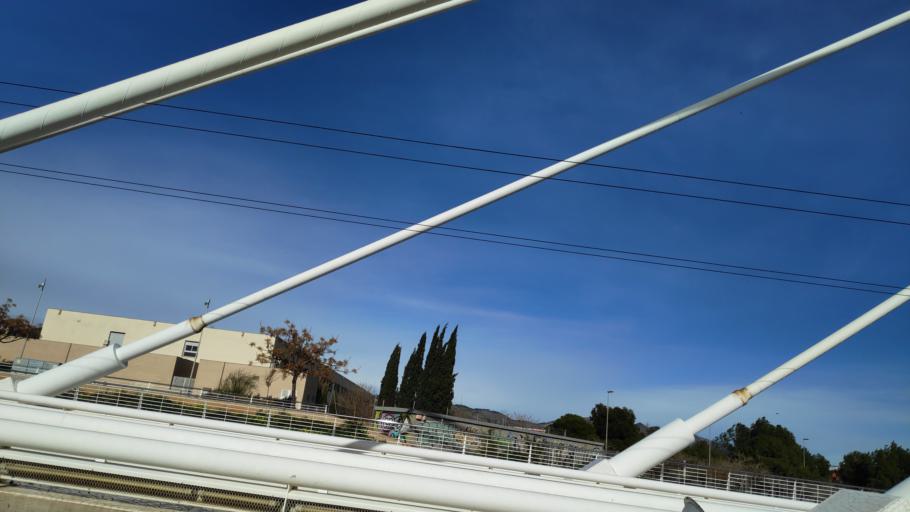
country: ES
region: Valencia
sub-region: Provincia de Castello
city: Castello de la Plana
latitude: 39.9909
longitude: -0.0563
